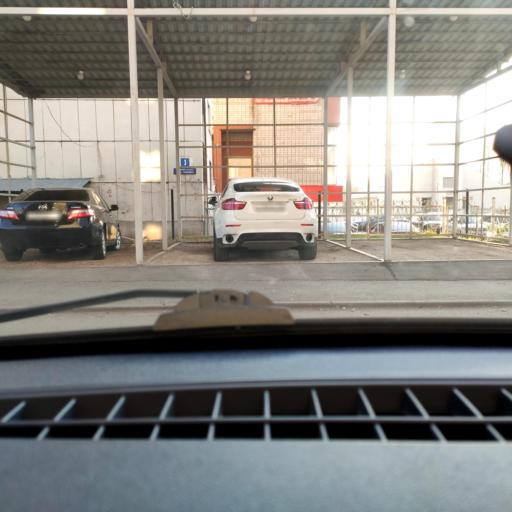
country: RU
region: Bashkortostan
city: Ufa
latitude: 54.7691
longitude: 56.0340
